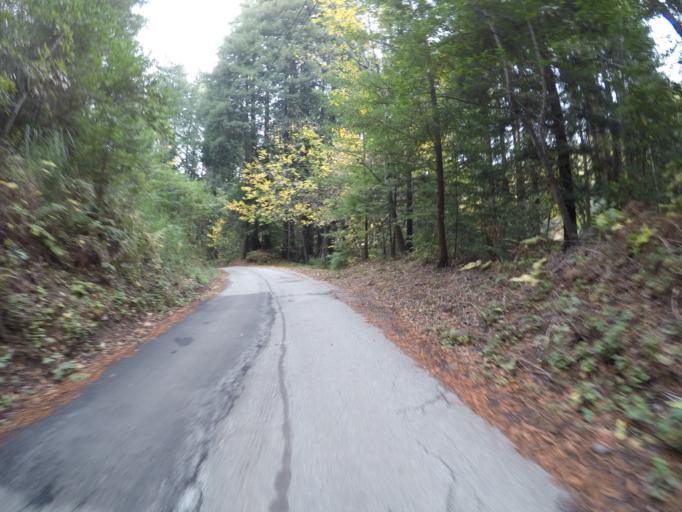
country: US
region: California
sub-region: Santa Cruz County
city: Scotts Valley
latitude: 37.0400
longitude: -121.9749
